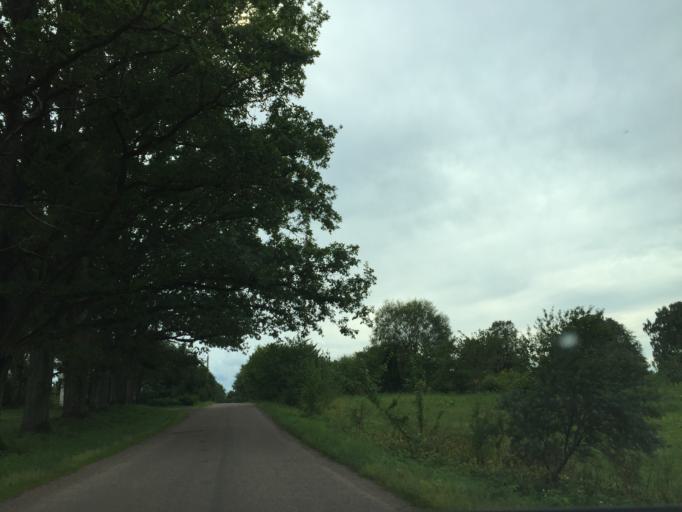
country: LV
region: Ogre
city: Ogre
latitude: 56.7702
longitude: 24.6599
